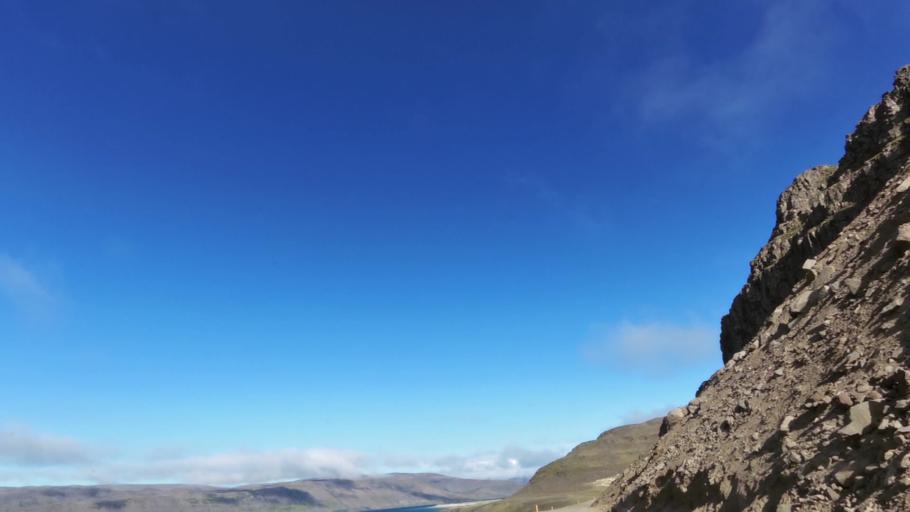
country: IS
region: West
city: Olafsvik
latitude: 65.5614
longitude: -24.0241
